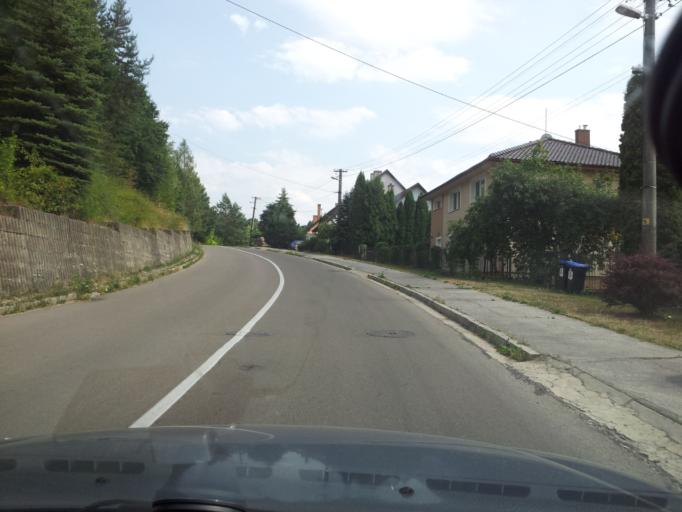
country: SK
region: Trenciansky
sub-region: Okres Trencin
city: Trencin
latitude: 48.8891
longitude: 18.0911
